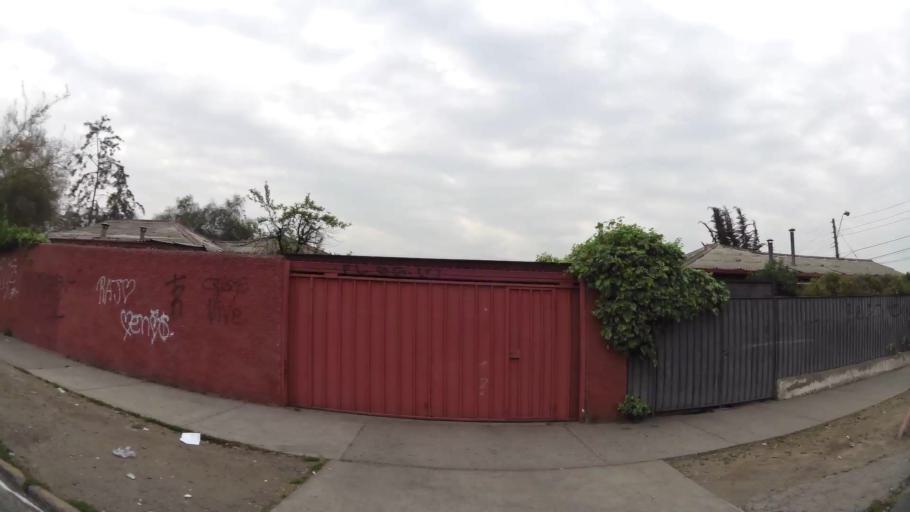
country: CL
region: Santiago Metropolitan
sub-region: Provincia de Santiago
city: Villa Presidente Frei, Nunoa, Santiago, Chile
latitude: -33.4906
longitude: -70.6017
